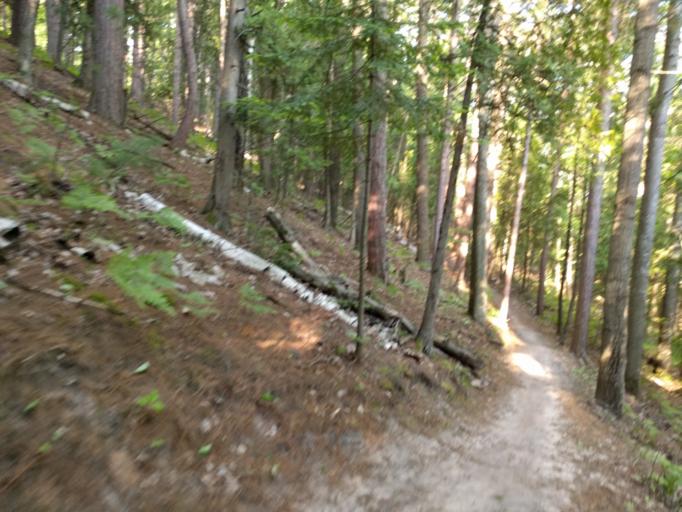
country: US
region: Michigan
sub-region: Marquette County
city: Trowbridge Park
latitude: 46.5691
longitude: -87.4523
